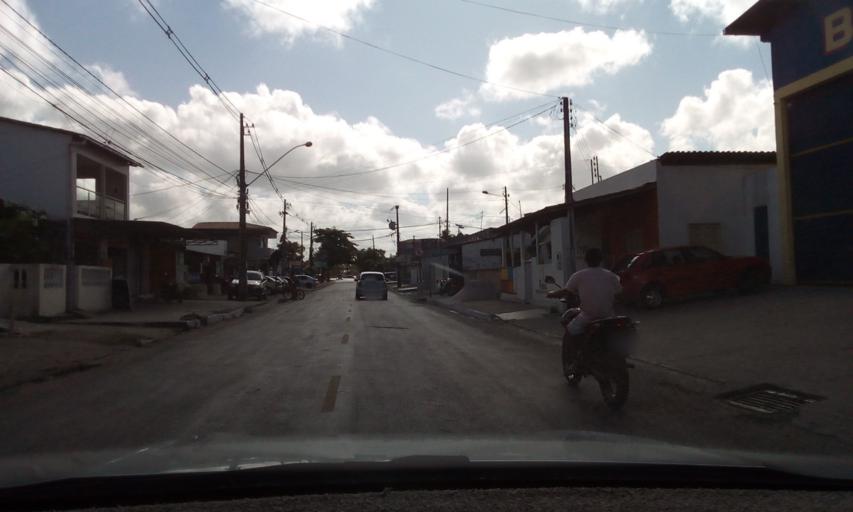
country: BR
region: Paraiba
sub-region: Bayeux
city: Bayeux
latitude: -7.1568
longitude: -34.9043
